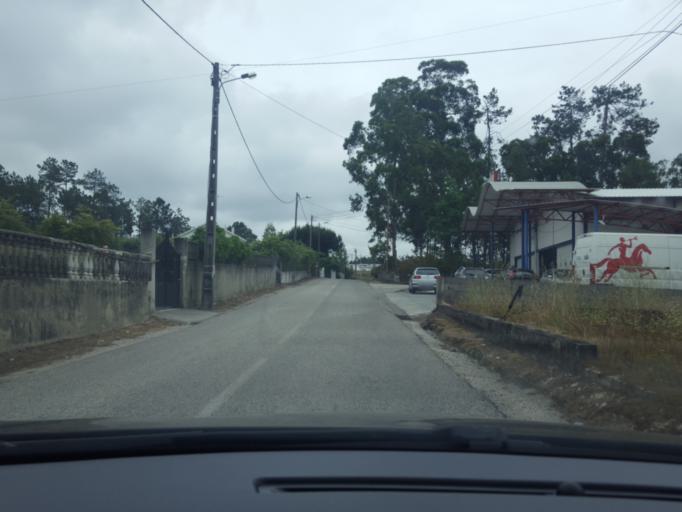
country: PT
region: Leiria
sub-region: Leiria
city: Caranguejeira
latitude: 39.7917
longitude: -8.7495
